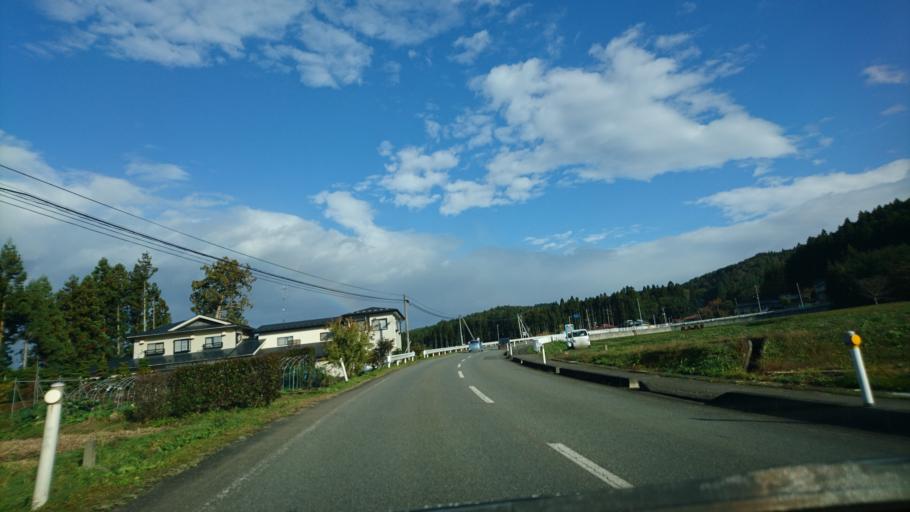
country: JP
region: Iwate
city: Mizusawa
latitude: 39.0411
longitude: 141.0608
